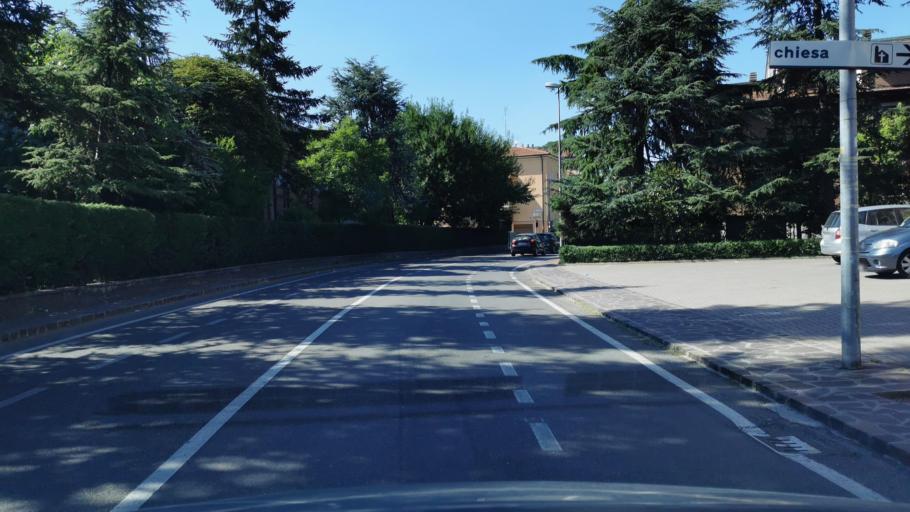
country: IT
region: Emilia-Romagna
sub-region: Provincia di Modena
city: Modena
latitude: 44.6236
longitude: 10.9272
